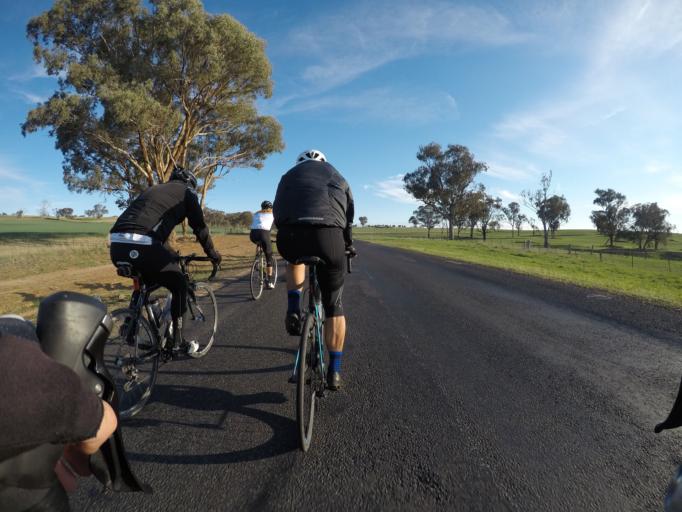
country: AU
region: New South Wales
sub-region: Cabonne
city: Molong
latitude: -32.9822
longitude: 148.7870
